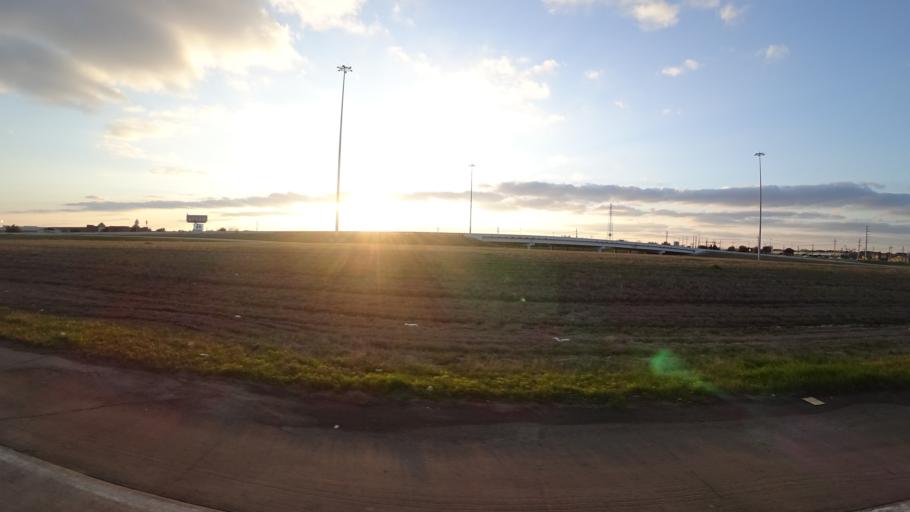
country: US
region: Texas
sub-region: Denton County
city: Lewisville
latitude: 33.0004
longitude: -96.9929
